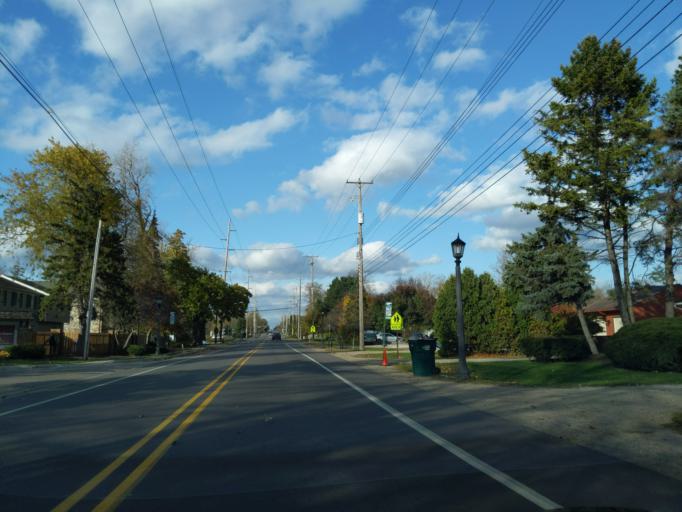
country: US
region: Michigan
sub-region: Ingham County
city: Lansing
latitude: 42.7570
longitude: -84.5231
